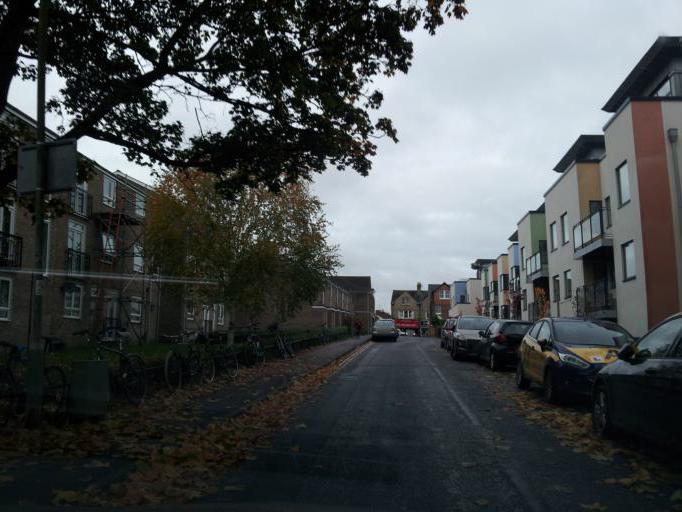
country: GB
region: England
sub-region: Oxfordshire
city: Oxford
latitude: 51.7598
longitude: -1.2682
